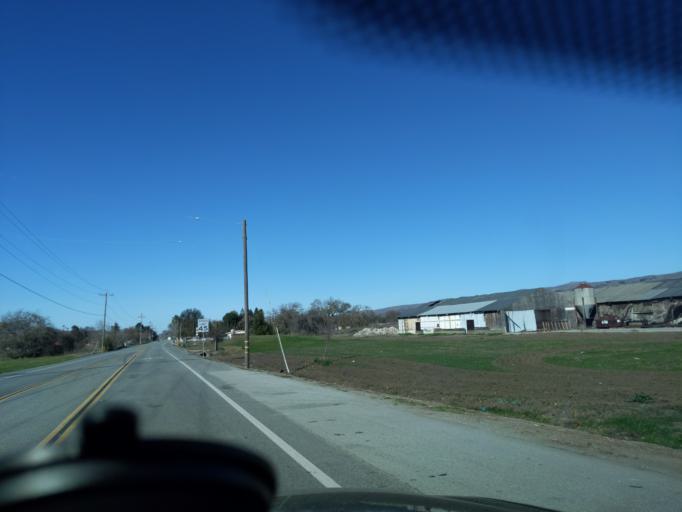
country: US
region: California
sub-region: Santa Clara County
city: Morgan Hill
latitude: 37.1700
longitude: -121.7092
